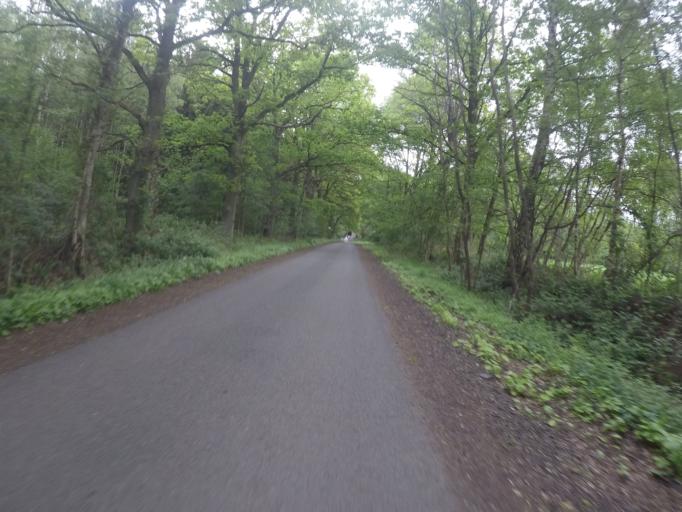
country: DE
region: Schleswig-Holstein
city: Bonningstedt
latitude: 53.6746
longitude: 9.9292
